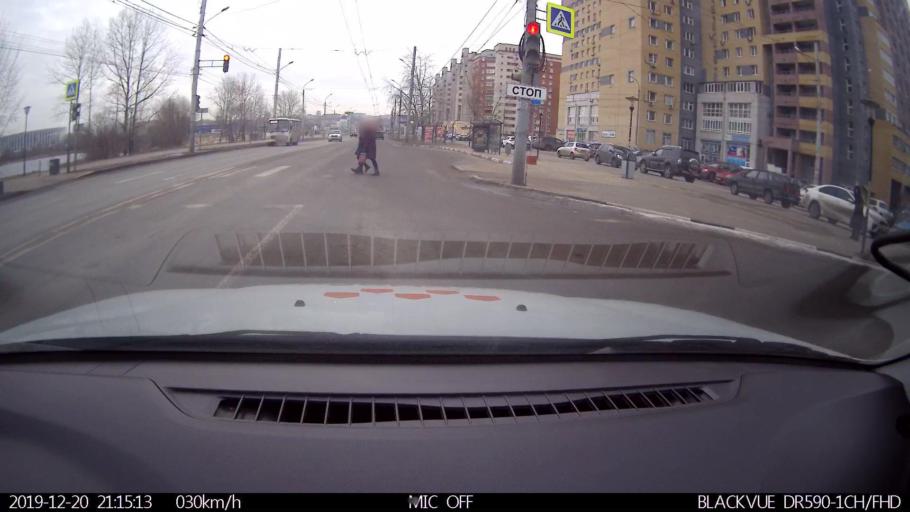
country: RU
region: Nizjnij Novgorod
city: Nizhniy Novgorod
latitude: 56.3361
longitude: 43.9410
